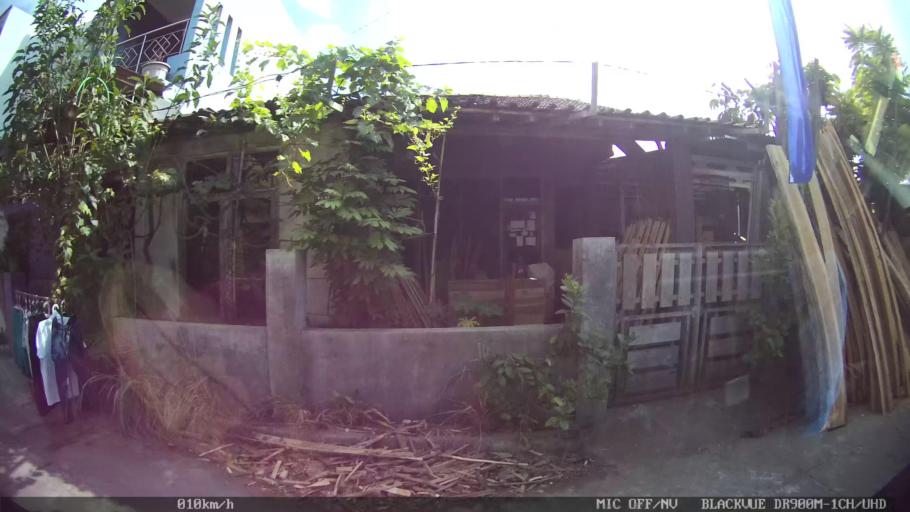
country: ID
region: Daerah Istimewa Yogyakarta
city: Kasihan
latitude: -7.8325
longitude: 110.3642
